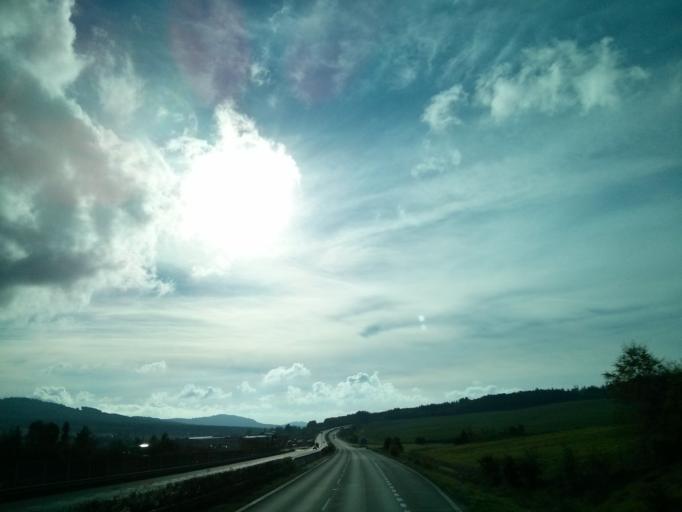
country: CZ
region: Plzensky
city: Myto
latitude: 49.7897
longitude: 13.7247
